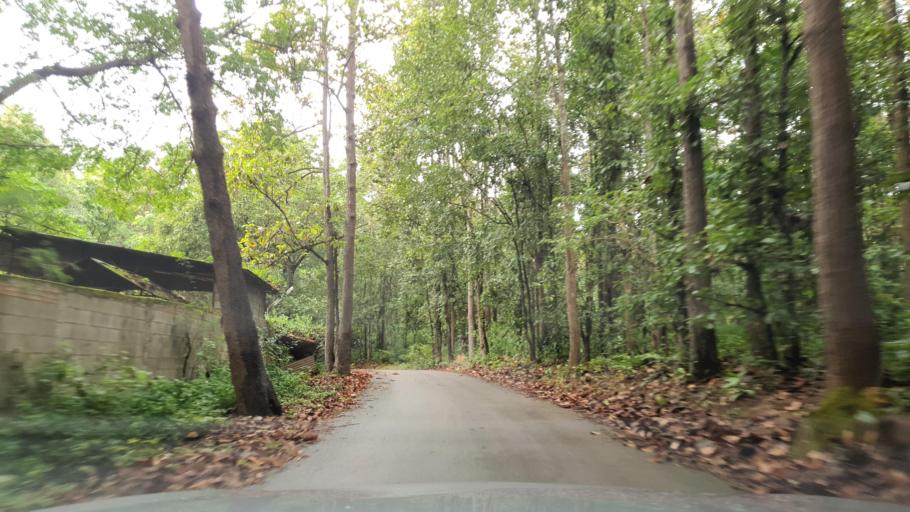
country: TH
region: Chiang Mai
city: Mae Taeng
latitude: 19.2054
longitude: 98.9344
